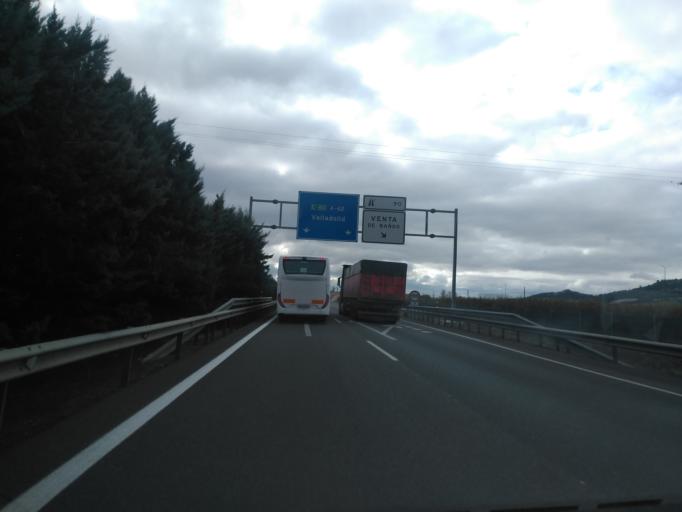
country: ES
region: Castille and Leon
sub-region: Provincia de Palencia
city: Venta de Banos
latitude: 41.9073
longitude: -4.5144
